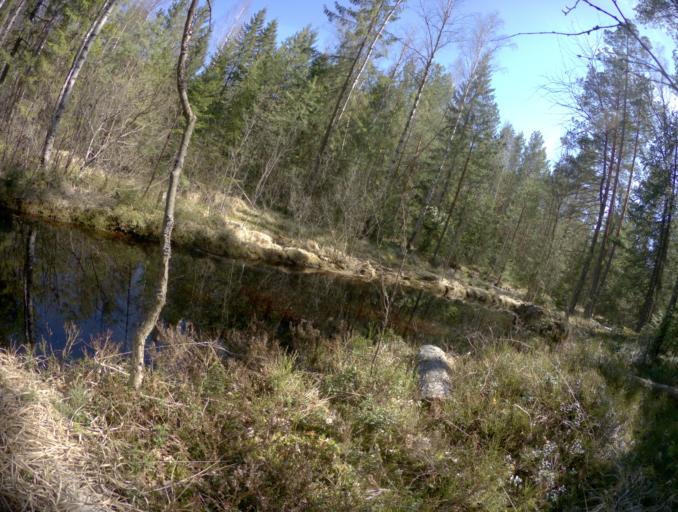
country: RU
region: Vladimir
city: Ivanishchi
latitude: 55.8279
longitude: 40.4239
